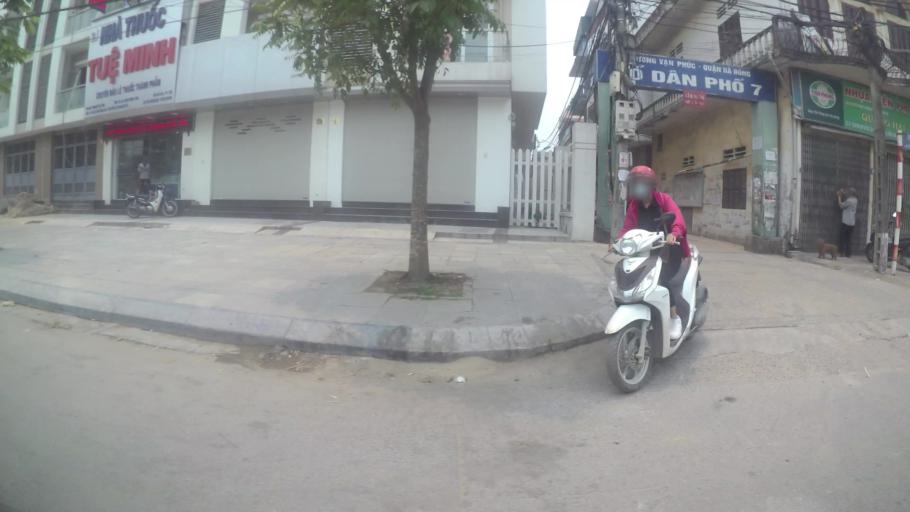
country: VN
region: Ha Noi
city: Ha Dong
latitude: 20.9776
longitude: 105.7751
